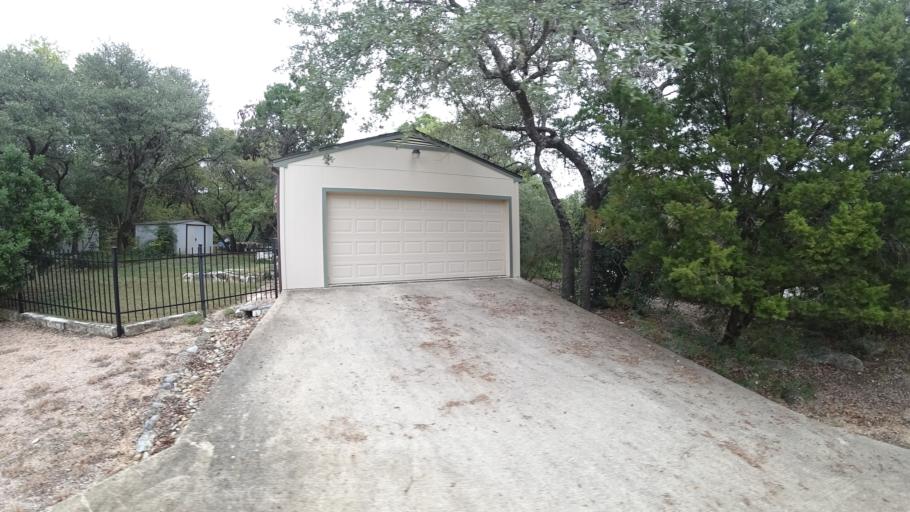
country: US
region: Texas
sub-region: Travis County
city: Hudson Bend
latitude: 30.3948
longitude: -97.9195
